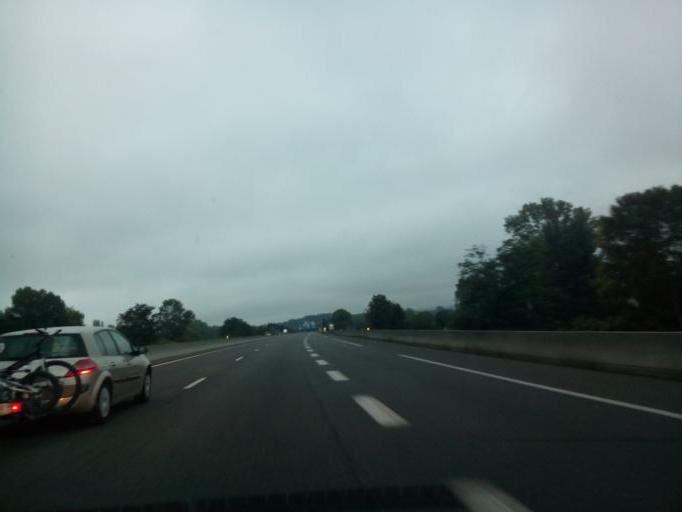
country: FR
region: Rhone-Alpes
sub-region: Departement de l'Isere
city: Ruy
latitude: 45.5707
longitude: 5.3336
